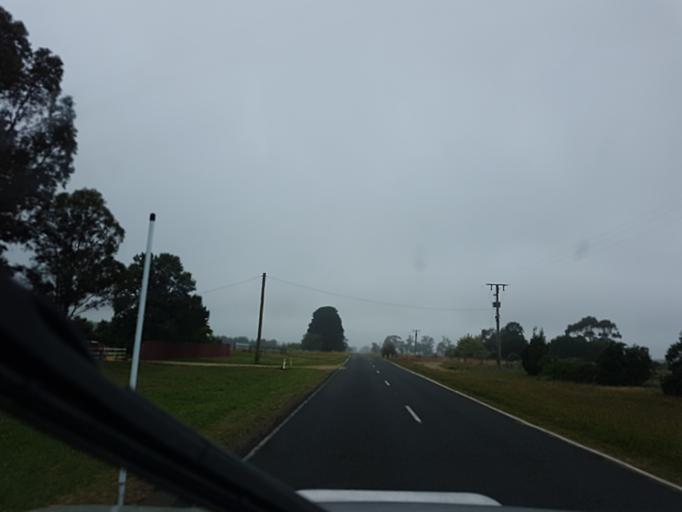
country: AU
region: Victoria
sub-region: Wellington
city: Sale
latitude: -38.0636
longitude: 147.0389
